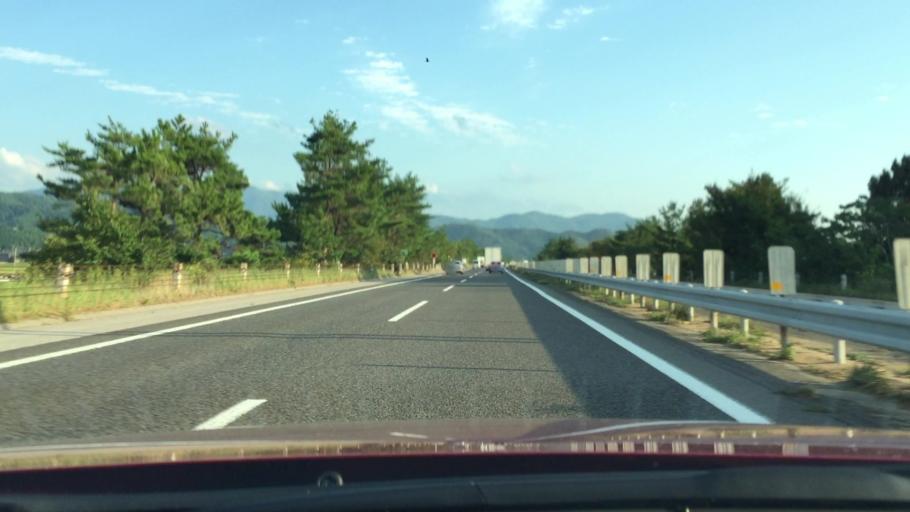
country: JP
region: Shiga Prefecture
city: Nagahama
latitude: 35.3779
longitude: 136.3020
